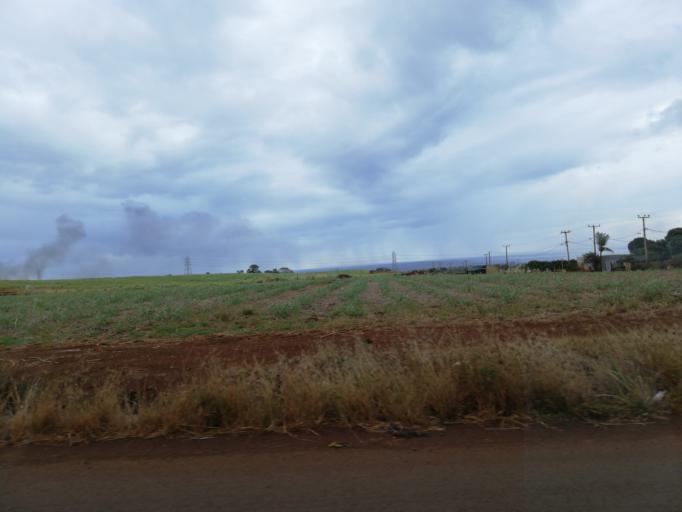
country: MU
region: Black River
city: Petite Riviere
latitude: -20.2083
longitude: 57.4552
